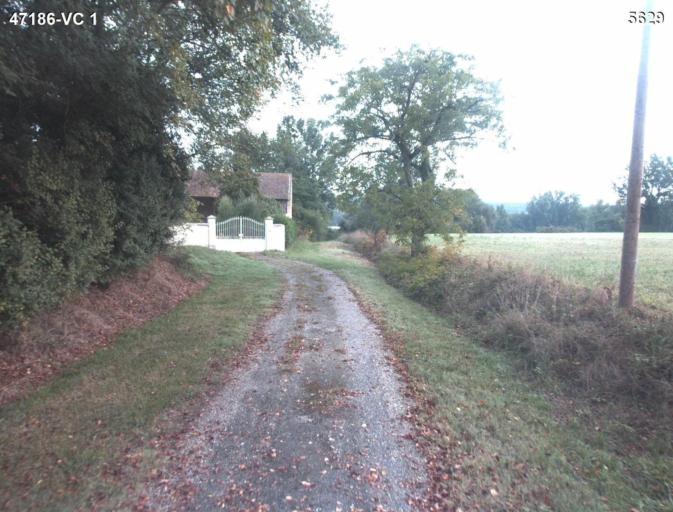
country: FR
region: Aquitaine
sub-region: Departement du Lot-et-Garonne
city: Port-Sainte-Marie
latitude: 44.2322
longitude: 0.4315
